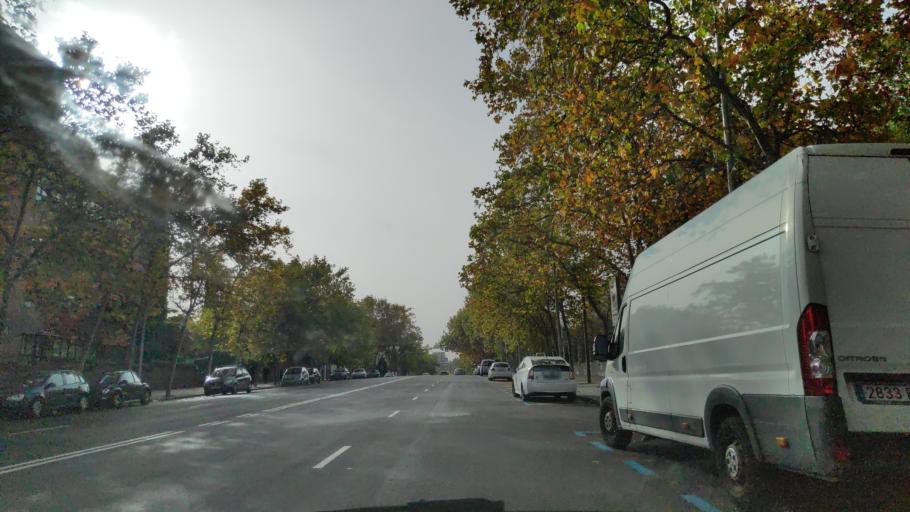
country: ES
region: Madrid
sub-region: Provincia de Madrid
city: Chamartin
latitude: 40.4662
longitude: -3.6858
